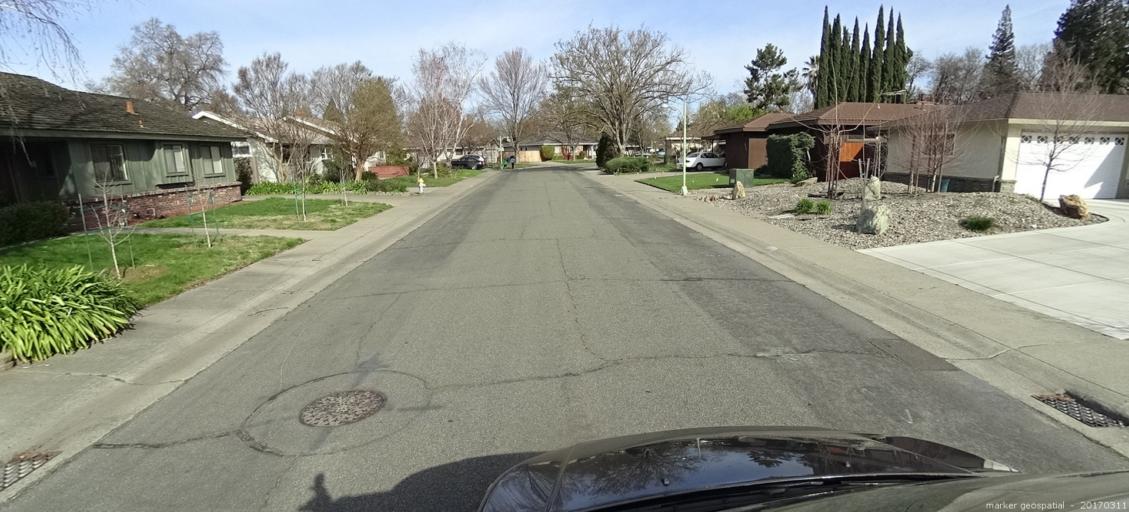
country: US
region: California
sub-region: Yolo County
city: West Sacramento
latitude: 38.5082
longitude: -121.5477
